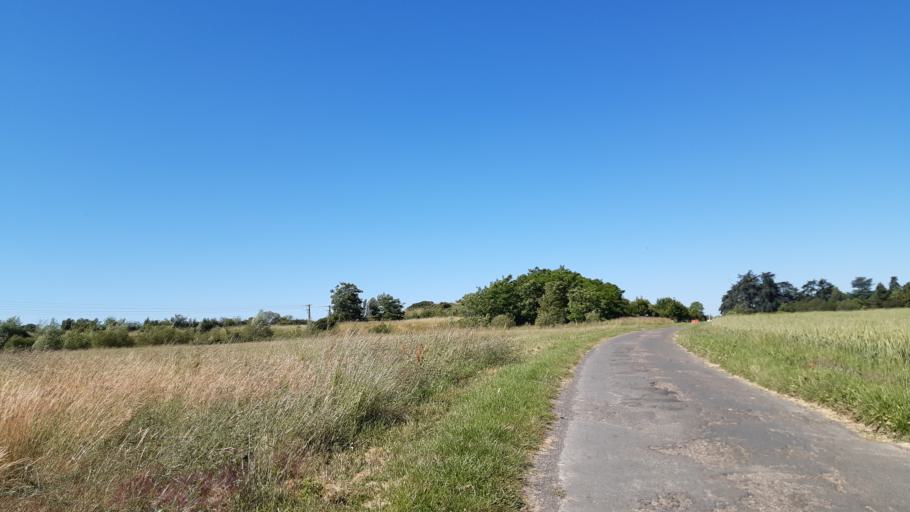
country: FR
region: Centre
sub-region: Departement d'Indre-et-Loire
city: Mettray
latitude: 47.4333
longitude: 0.6534
